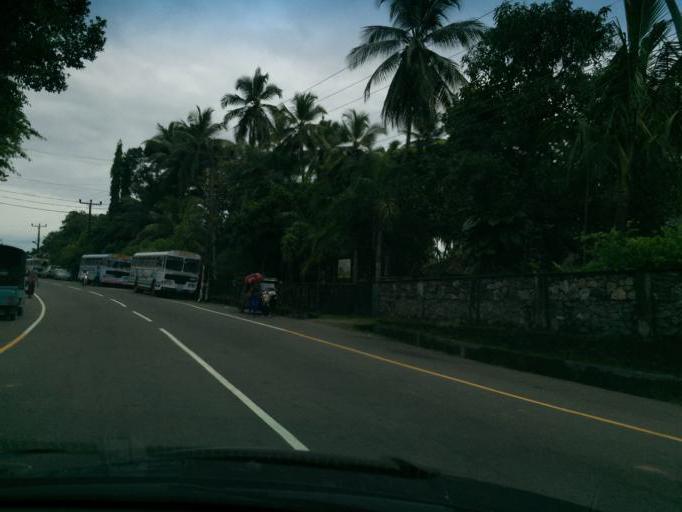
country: LK
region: Western
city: Horana South
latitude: 6.7137
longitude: 80.0634
